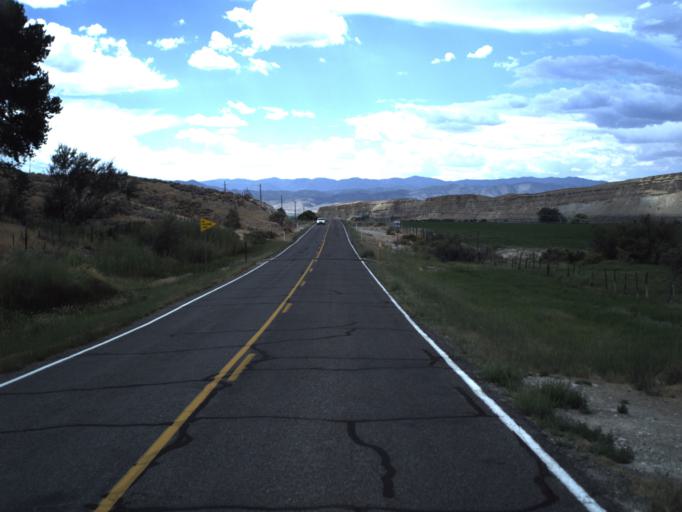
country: US
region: Utah
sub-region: Sanpete County
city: Gunnison
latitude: 39.1457
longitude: -111.7485
